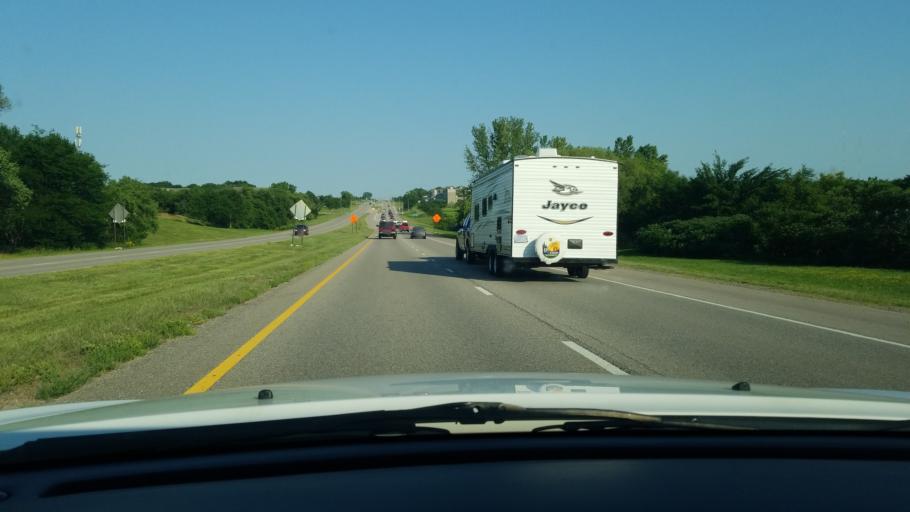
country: US
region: Nebraska
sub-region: Lancaster County
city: Lincoln
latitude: 40.7447
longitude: -96.6228
